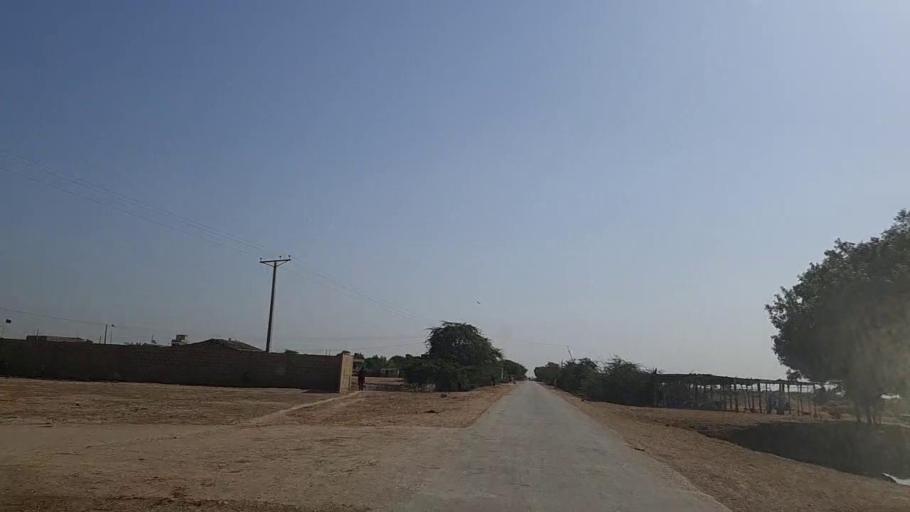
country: PK
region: Sindh
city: Mirpur Batoro
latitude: 24.6412
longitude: 68.2907
